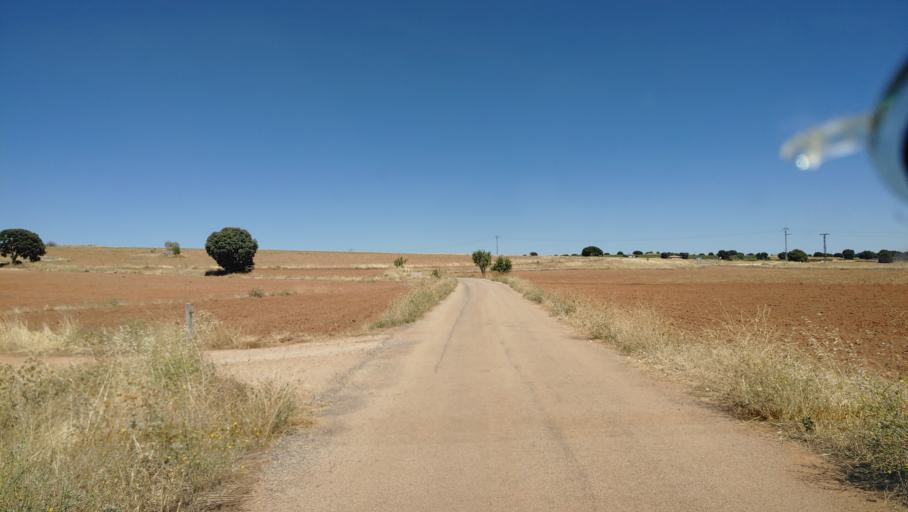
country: ES
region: Castille-La Mancha
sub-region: Provincia de Albacete
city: Ossa de Montiel
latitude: 38.9342
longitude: -2.7548
